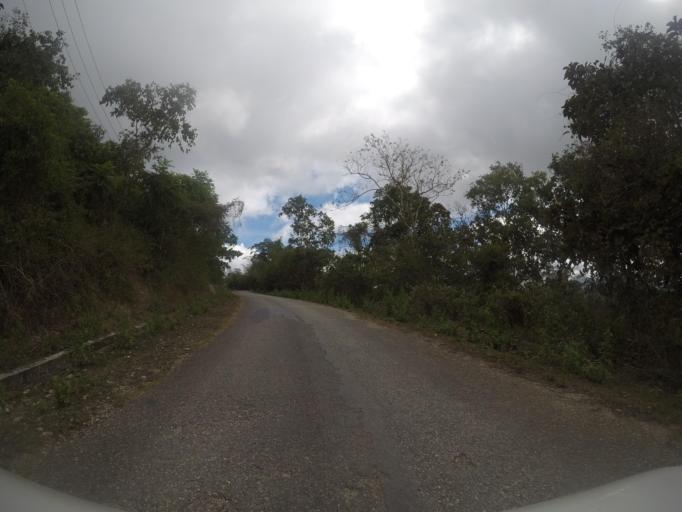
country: TL
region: Lautem
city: Lospalos
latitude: -8.5430
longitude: 126.9051
